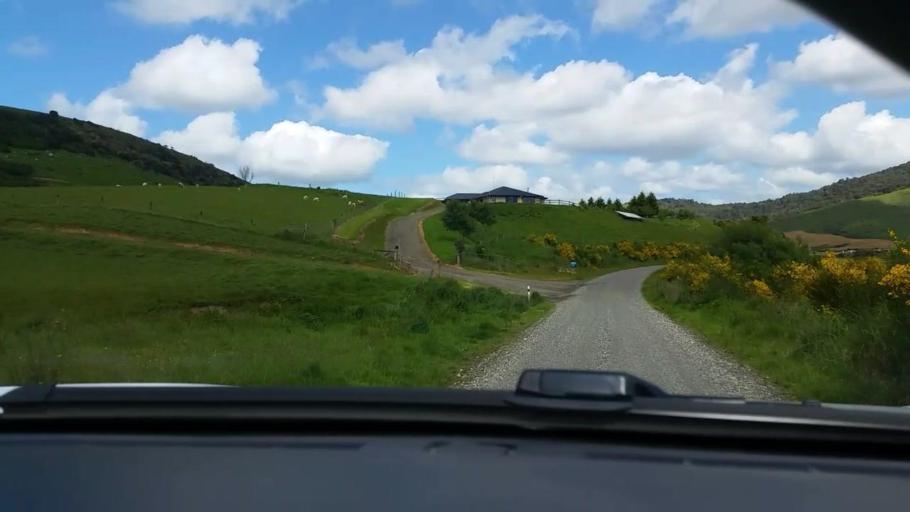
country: NZ
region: Otago
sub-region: Clutha District
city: Papatowai
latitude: -46.5902
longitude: 169.1472
